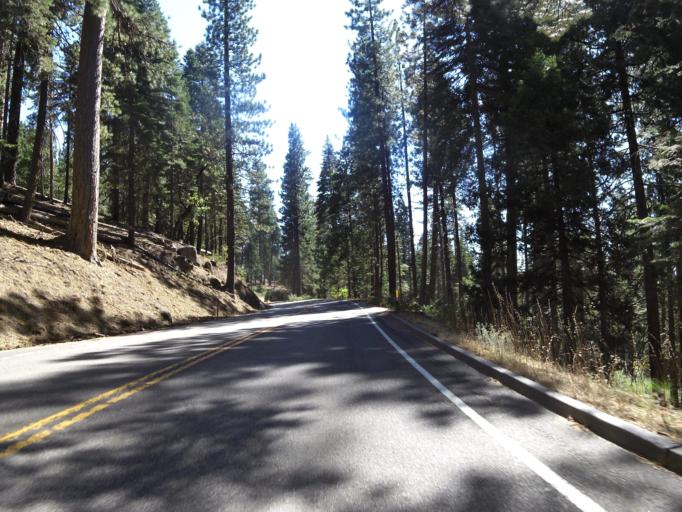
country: US
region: California
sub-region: Mariposa County
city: Yosemite Valley
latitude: 37.6324
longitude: -119.6859
